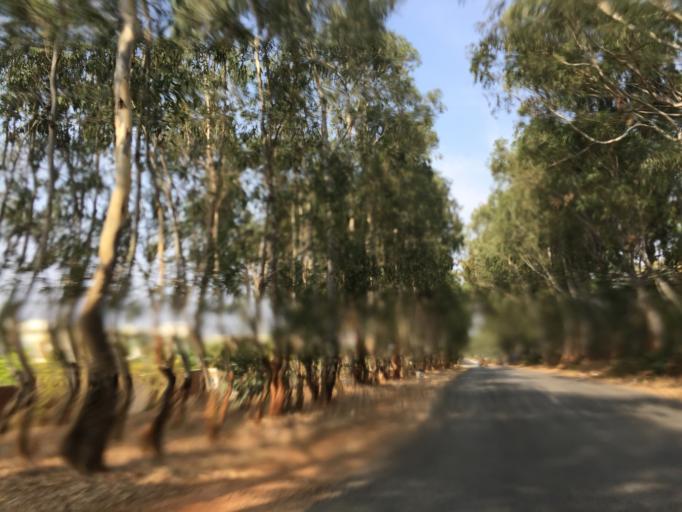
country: IN
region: Karnataka
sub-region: Chikkaballapur
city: Chik Ballapur
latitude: 13.3483
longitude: 77.6688
